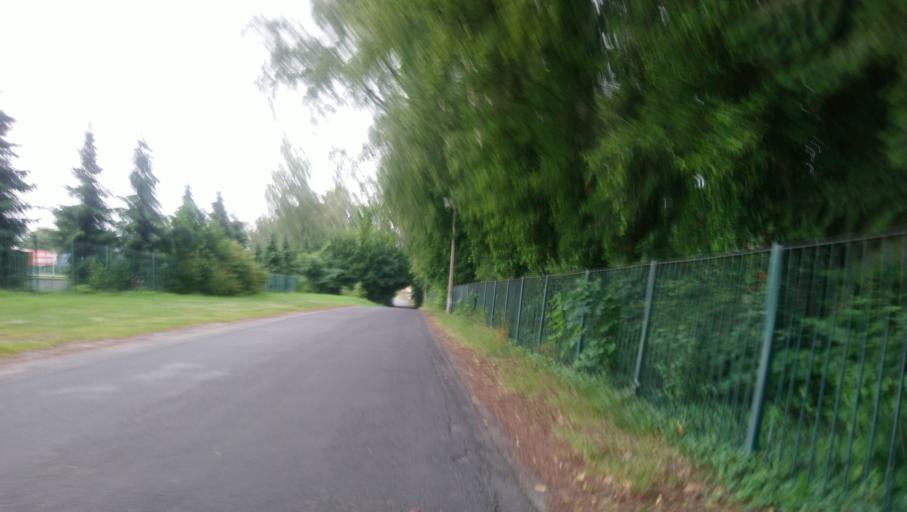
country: DE
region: Mecklenburg-Vorpommern
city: Kritzmow
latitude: 54.0689
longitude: 12.0971
